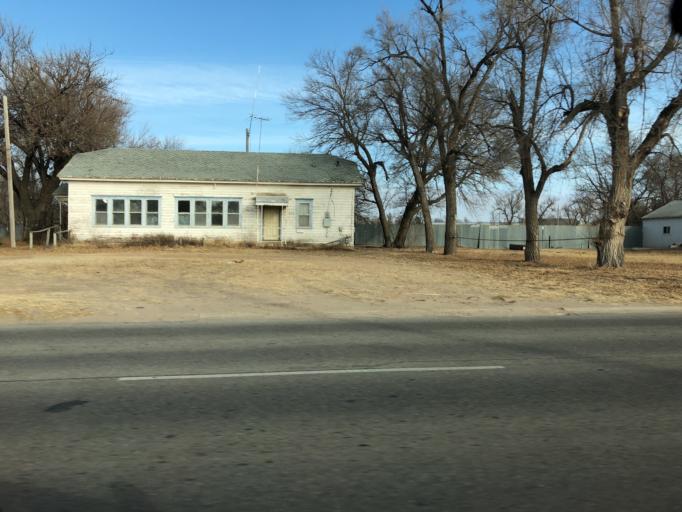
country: US
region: Kansas
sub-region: Reno County
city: Hutchinson
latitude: 38.0571
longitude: -97.9519
